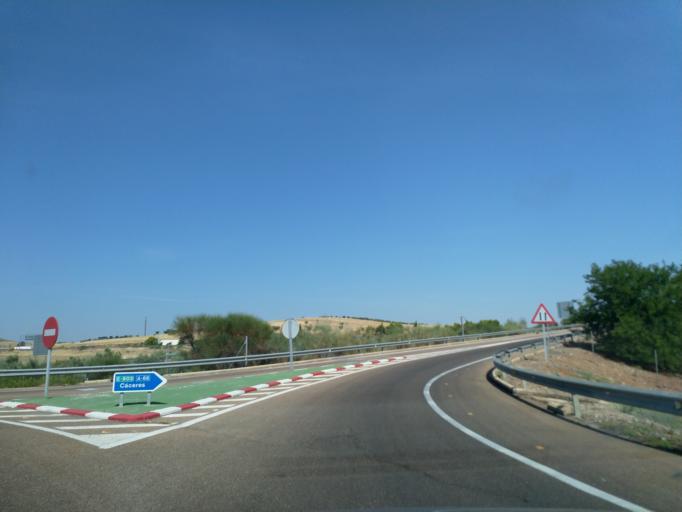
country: ES
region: Extremadura
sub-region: Provincia de Badajoz
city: Merida
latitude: 38.9405
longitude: -6.3431
